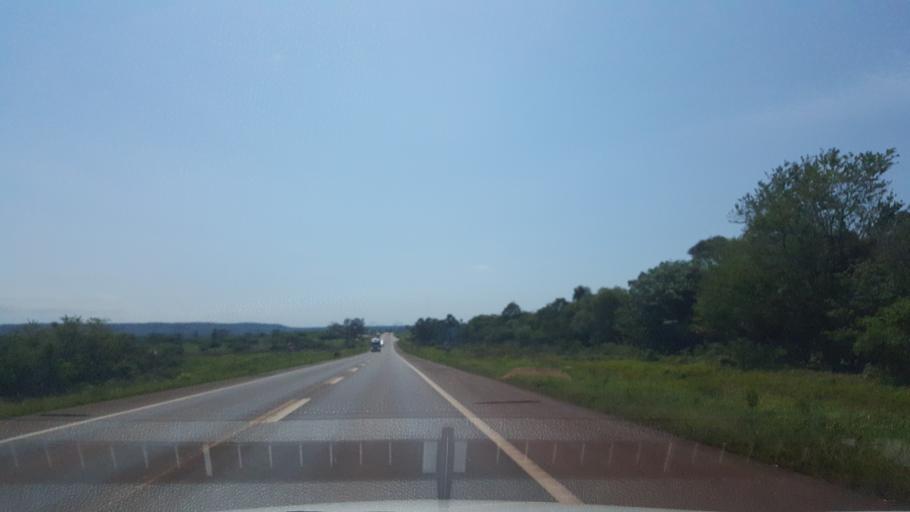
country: AR
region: Misiones
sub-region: Departamento de Apostoles
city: San Jose
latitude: -27.7860
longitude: -55.8267
